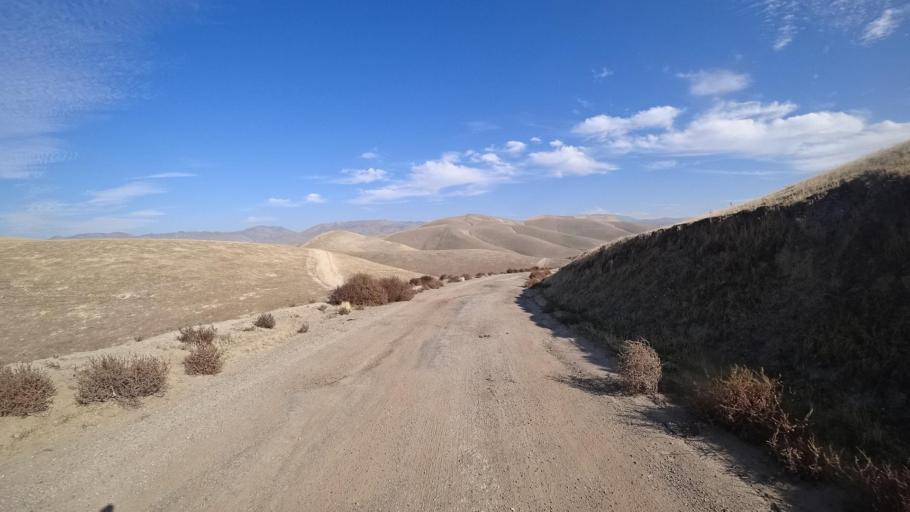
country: US
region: California
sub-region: Kern County
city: Oildale
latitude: 35.4968
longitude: -118.8638
